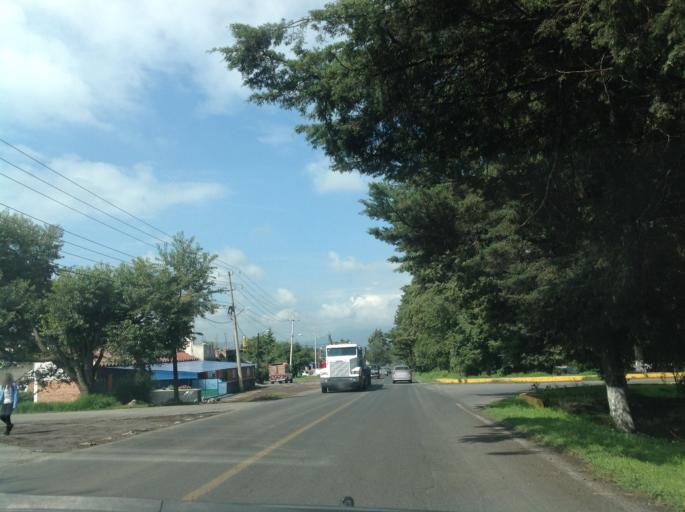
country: MX
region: Mexico
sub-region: Xalatlaco
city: Mezapa la Fabrica
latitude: 19.1790
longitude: -99.4436
